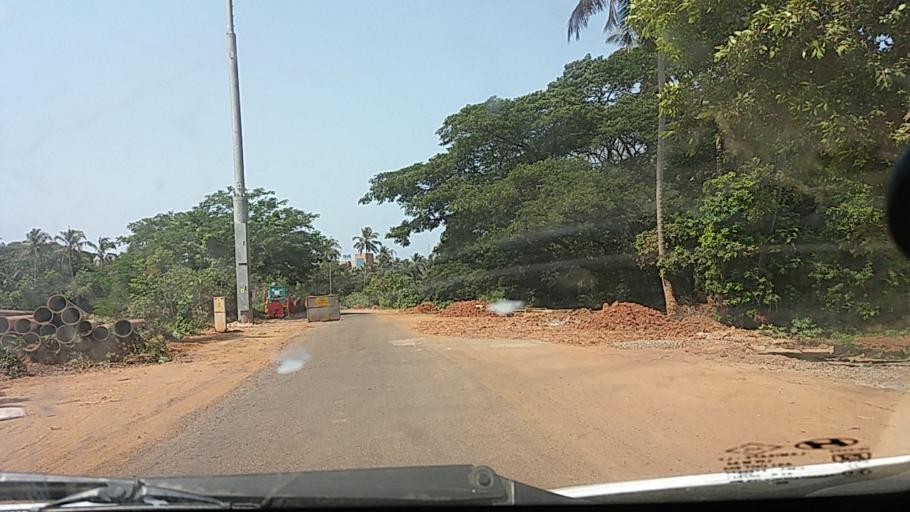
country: IN
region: Goa
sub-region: South Goa
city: Madgaon
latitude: 15.2808
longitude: 73.9547
